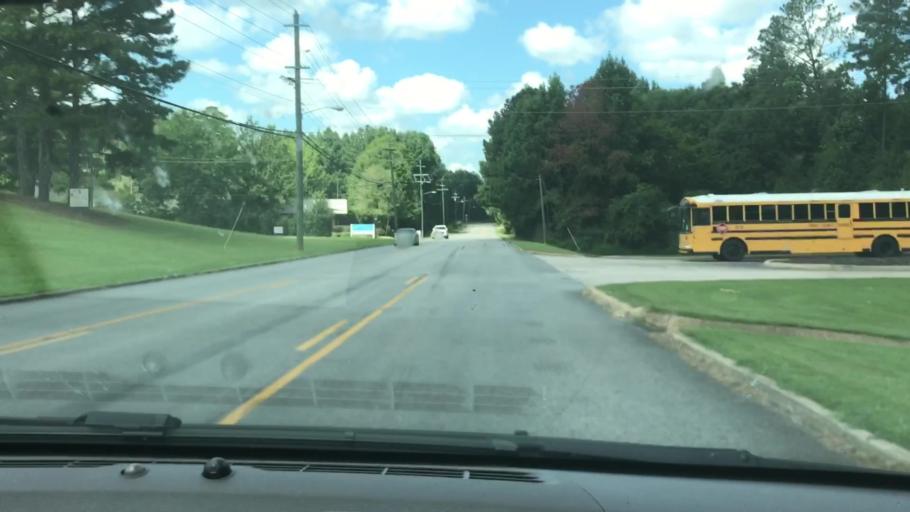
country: US
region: Georgia
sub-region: Troup County
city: La Grange
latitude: 32.9977
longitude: -85.0465
